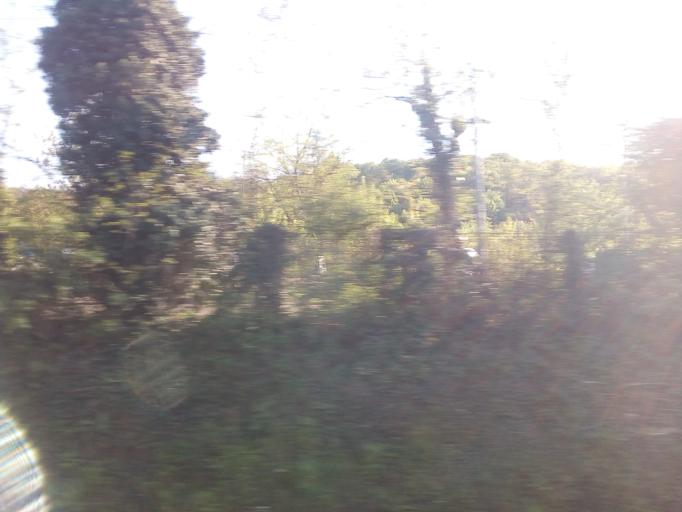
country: FR
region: Rhone-Alpes
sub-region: Departement de l'Isere
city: La Verpilliere
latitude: 45.6268
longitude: 5.1525
